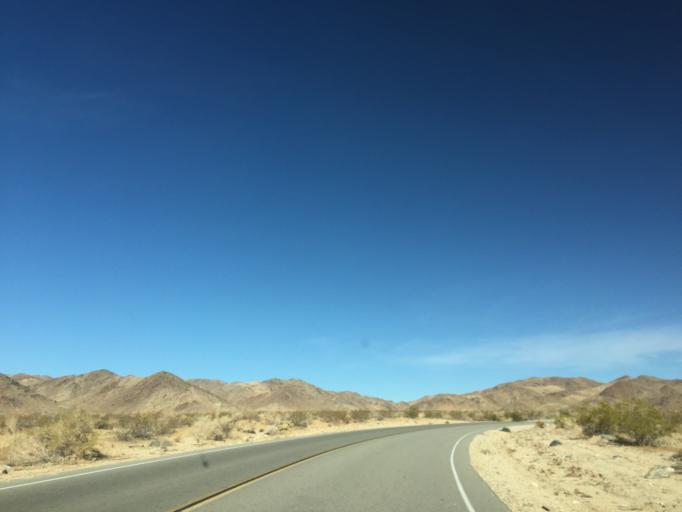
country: US
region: California
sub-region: San Bernardino County
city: Twentynine Palms
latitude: 33.9271
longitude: -115.9407
